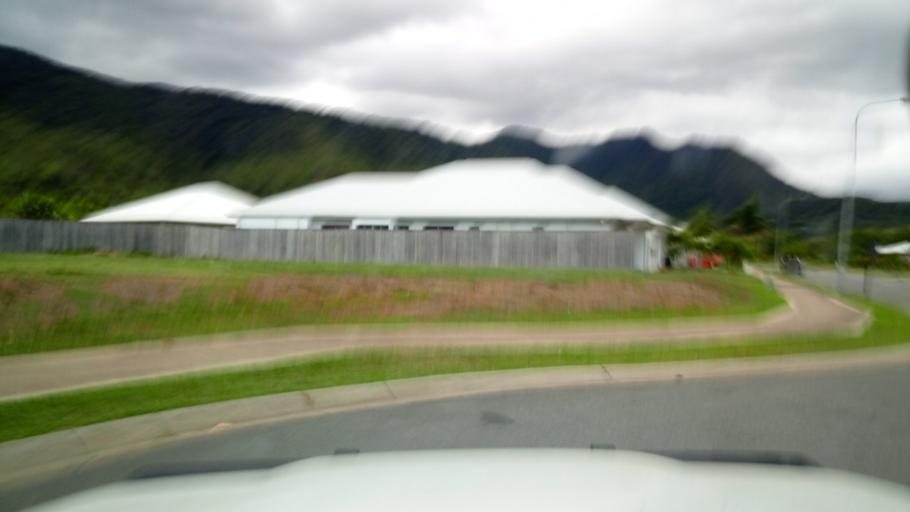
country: AU
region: Queensland
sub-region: Cairns
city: Redlynch
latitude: -16.8436
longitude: 145.6937
